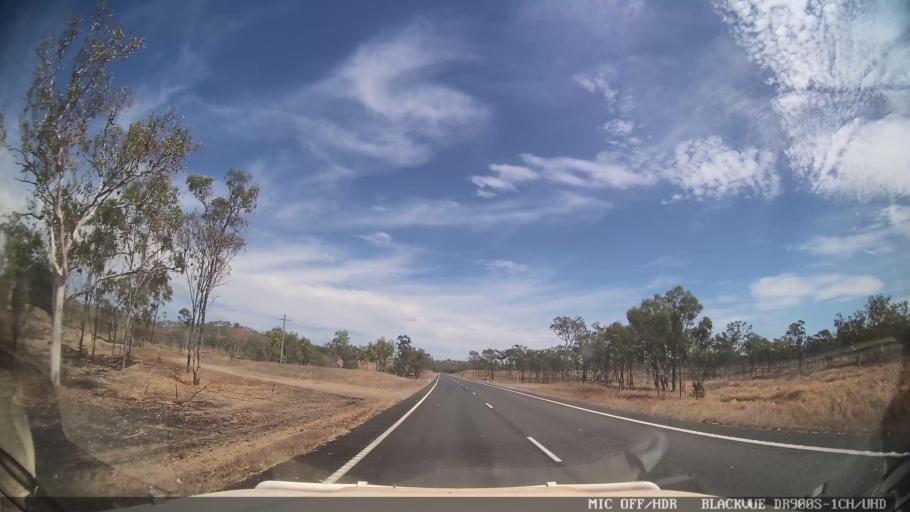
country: AU
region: Queensland
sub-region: Cook
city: Cooktown
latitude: -15.7581
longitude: 145.0002
